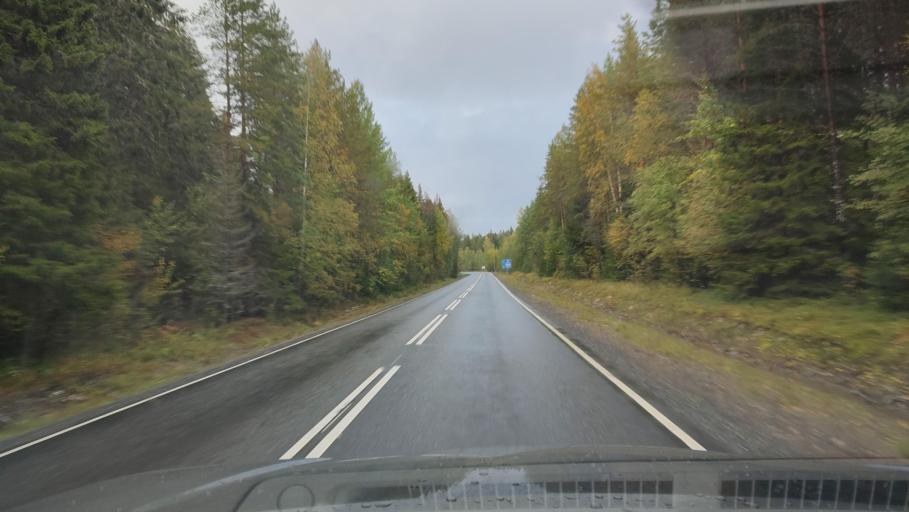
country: FI
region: Southern Ostrobothnia
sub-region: Suupohja
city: Karijoki
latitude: 62.2818
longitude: 21.6177
